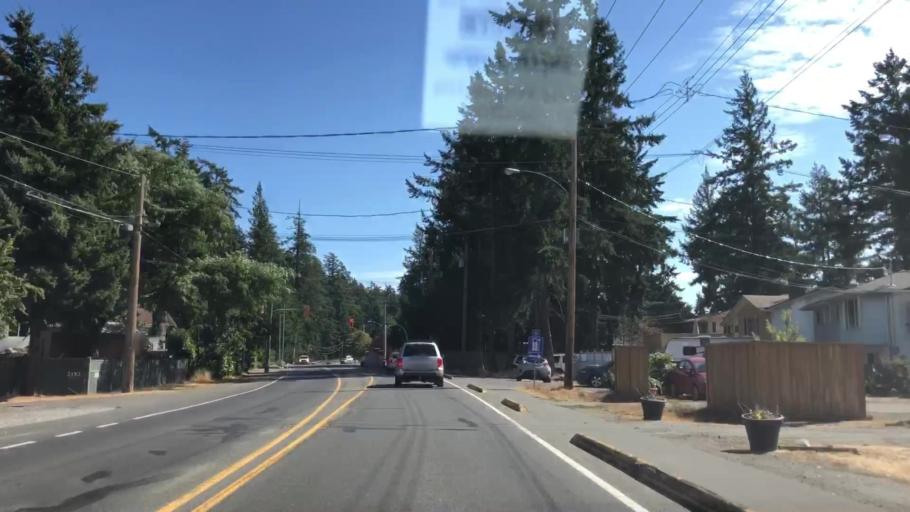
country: CA
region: British Columbia
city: Colwood
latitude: 48.4271
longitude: -123.4916
